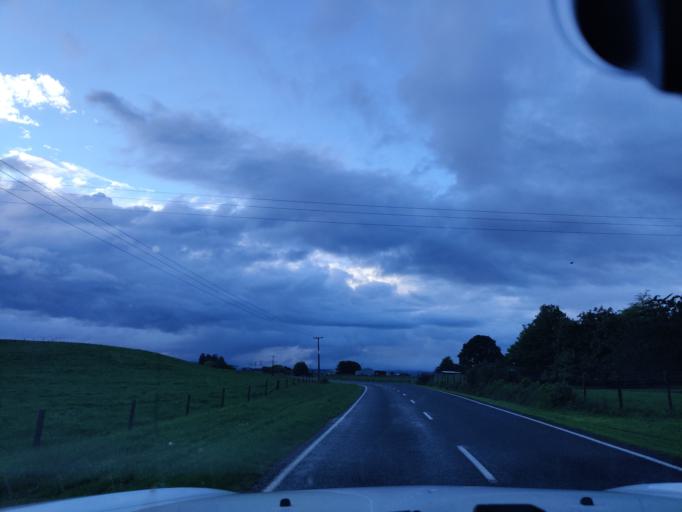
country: NZ
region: Waikato
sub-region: South Waikato District
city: Tokoroa
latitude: -38.2327
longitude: 175.8372
